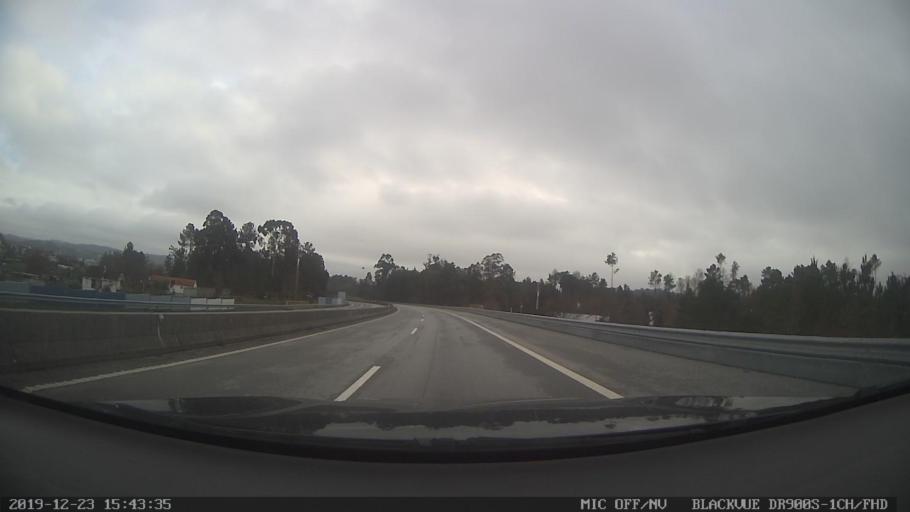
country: PT
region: Viseu
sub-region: Viseu
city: Abraveses
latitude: 40.6649
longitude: -7.9700
